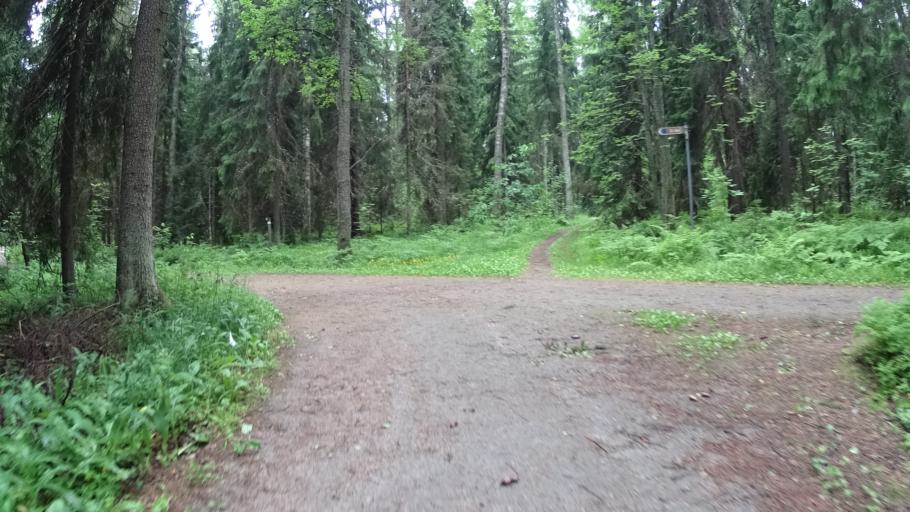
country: FI
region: Uusimaa
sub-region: Helsinki
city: Helsinki
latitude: 60.2628
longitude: 24.9095
